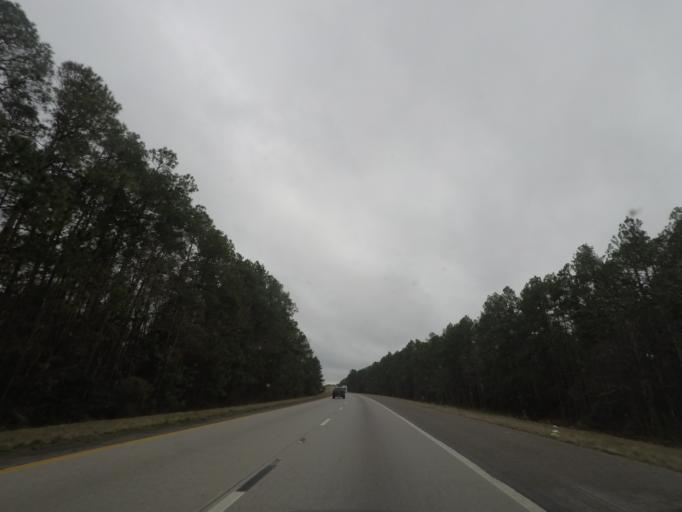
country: US
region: South Carolina
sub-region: Colleton County
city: Walterboro
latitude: 33.0424
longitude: -80.6700
